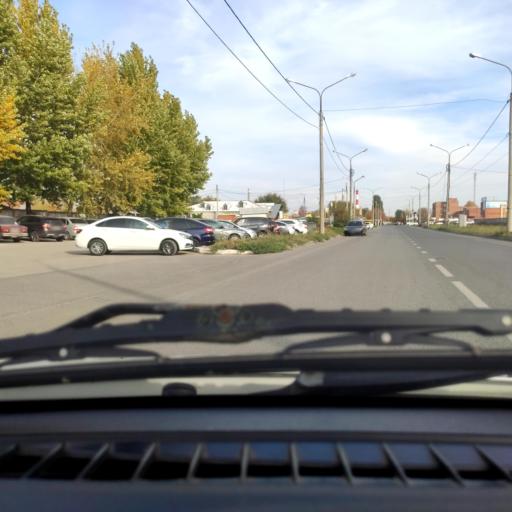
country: RU
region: Samara
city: Tol'yatti
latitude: 53.5418
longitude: 49.4196
